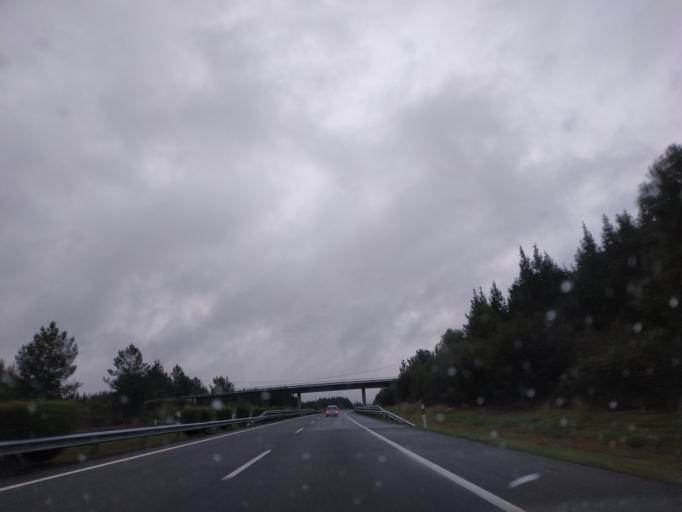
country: ES
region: Galicia
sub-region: Provincia de Lugo
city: Outeiro de Rei
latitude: 43.0928
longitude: -7.5892
